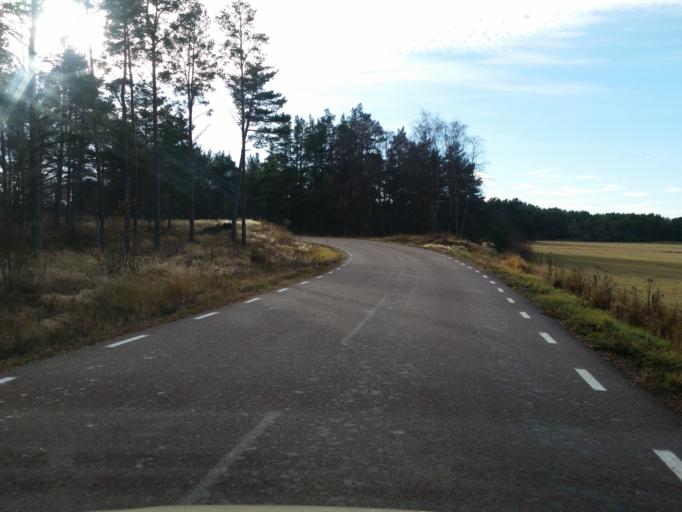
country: AX
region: Alands skaergard
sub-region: Kumlinge
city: Kumlinge
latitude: 60.2706
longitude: 20.7901
